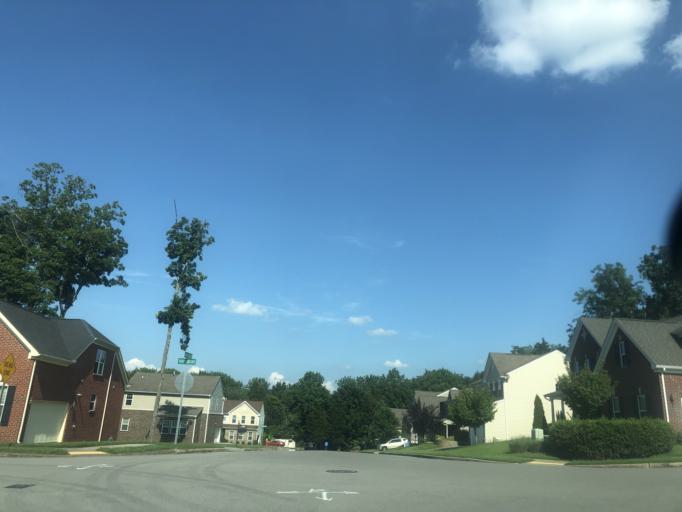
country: US
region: Tennessee
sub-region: Wilson County
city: Green Hill
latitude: 36.1463
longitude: -86.5900
